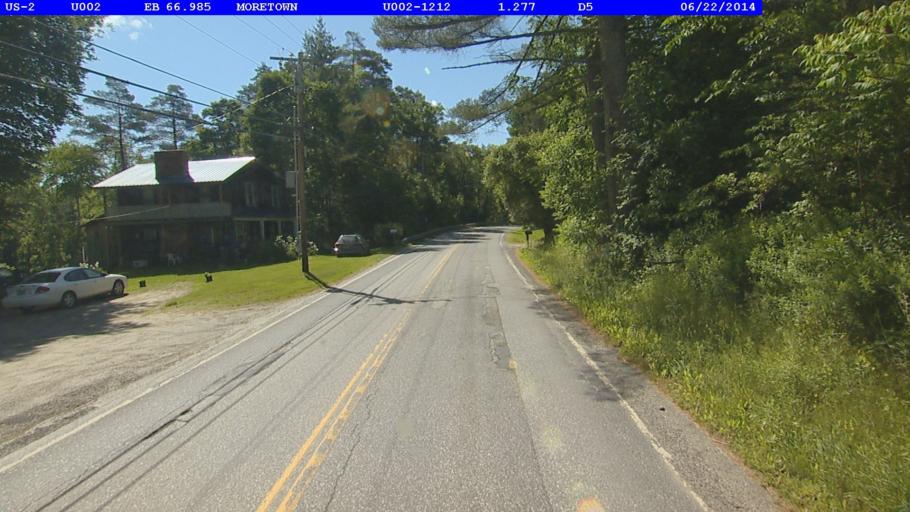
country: US
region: Vermont
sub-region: Washington County
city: Waterbury
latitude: 44.3160
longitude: -72.7265
